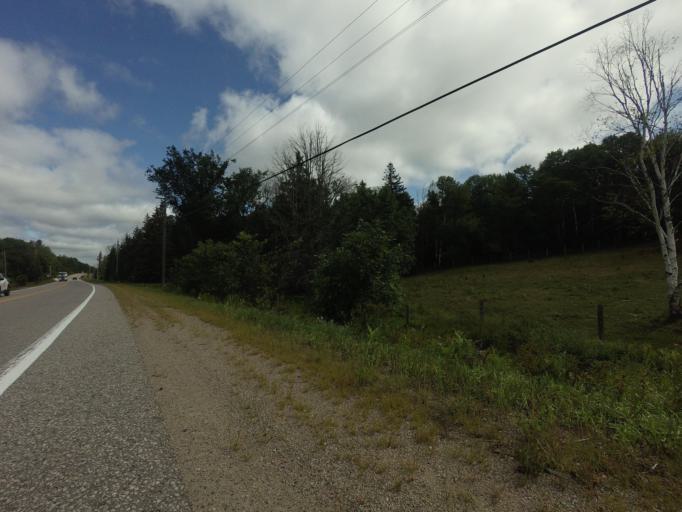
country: CA
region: Ontario
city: Omemee
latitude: 44.8246
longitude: -78.5641
